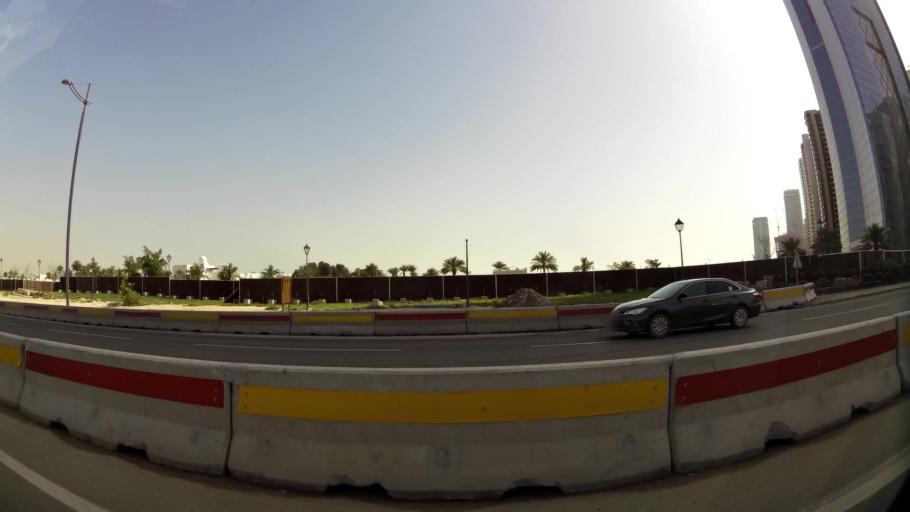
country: QA
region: Baladiyat ad Dawhah
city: Doha
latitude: 25.3307
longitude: 51.5228
